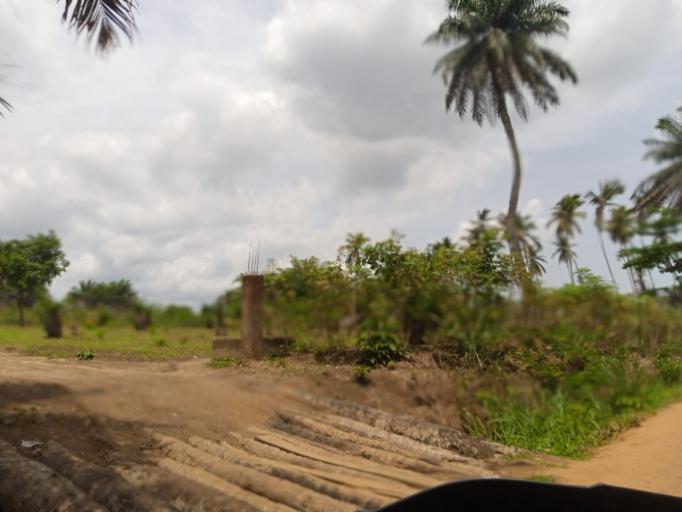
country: SL
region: Western Area
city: Waterloo
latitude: 8.3282
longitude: -13.0032
